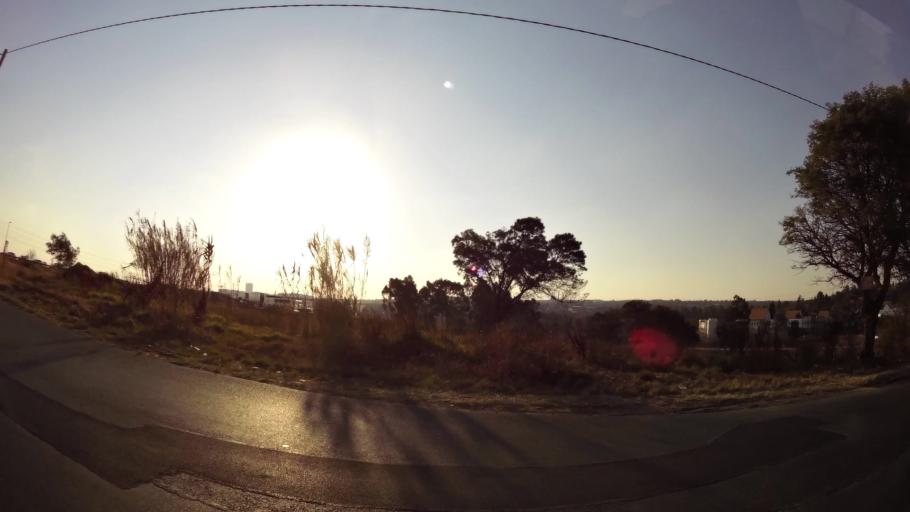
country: ZA
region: Gauteng
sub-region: City of Johannesburg Metropolitan Municipality
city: Midrand
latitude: -26.0322
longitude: 28.1383
